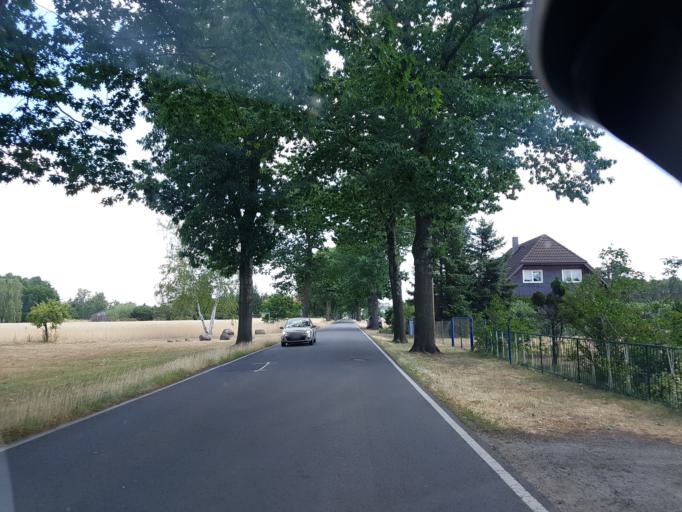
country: DE
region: Brandenburg
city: Cottbus
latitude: 51.7202
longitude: 14.3922
